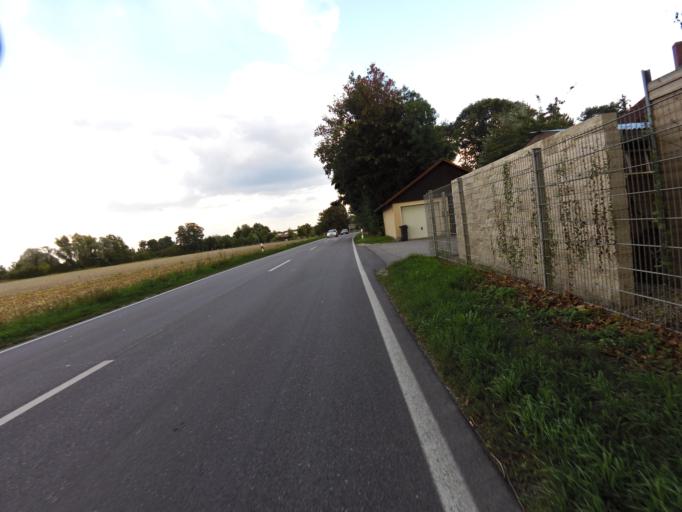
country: DE
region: Bavaria
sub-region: Upper Bavaria
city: Moosburg
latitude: 48.4651
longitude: 11.9577
